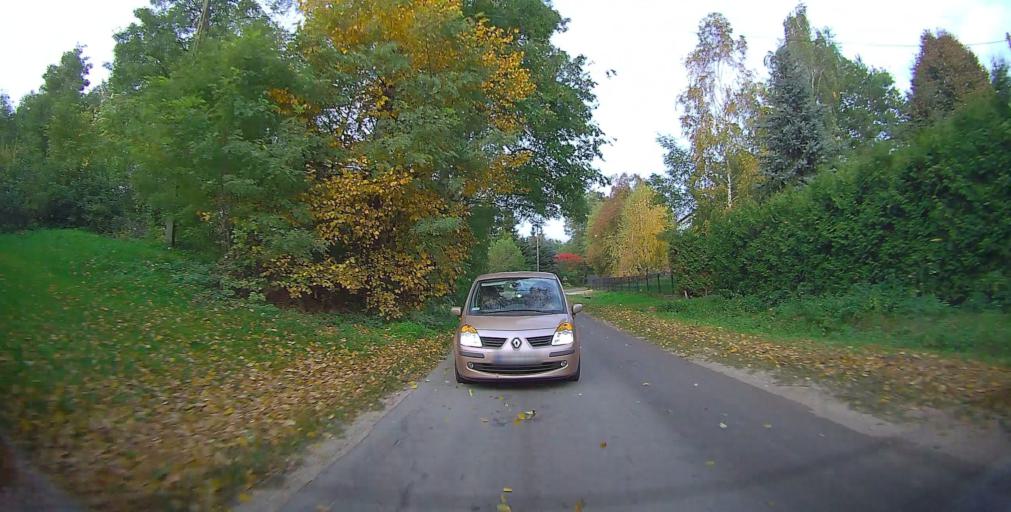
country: PL
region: Masovian Voivodeship
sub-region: Powiat grojecki
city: Mogielnica
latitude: 51.6434
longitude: 20.7398
